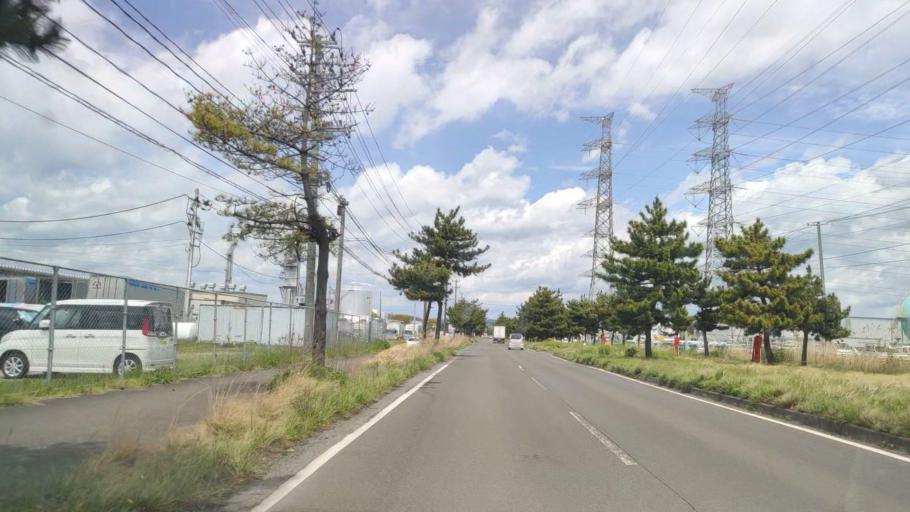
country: JP
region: Miyagi
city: Shiogama
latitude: 38.2844
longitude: 141.0246
